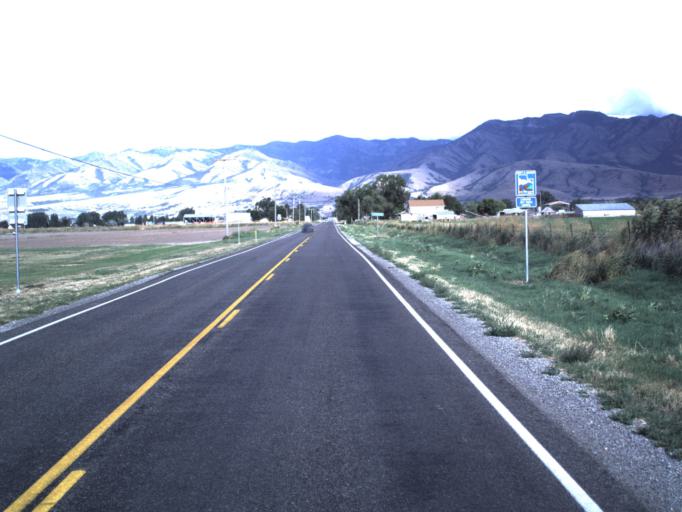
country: US
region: Utah
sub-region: Cache County
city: Lewiston
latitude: 41.9757
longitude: -111.8754
